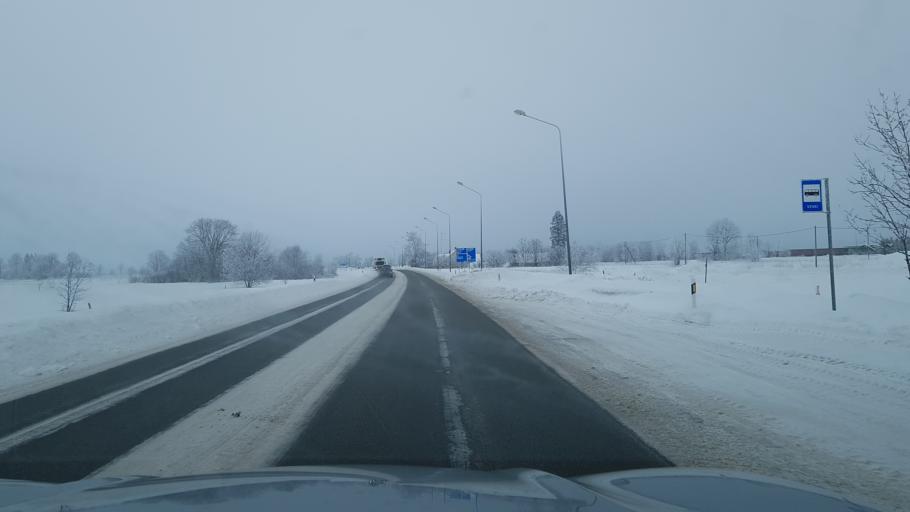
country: EE
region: Ida-Virumaa
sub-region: Johvi vald
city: Johvi
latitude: 59.3334
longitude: 27.4031
